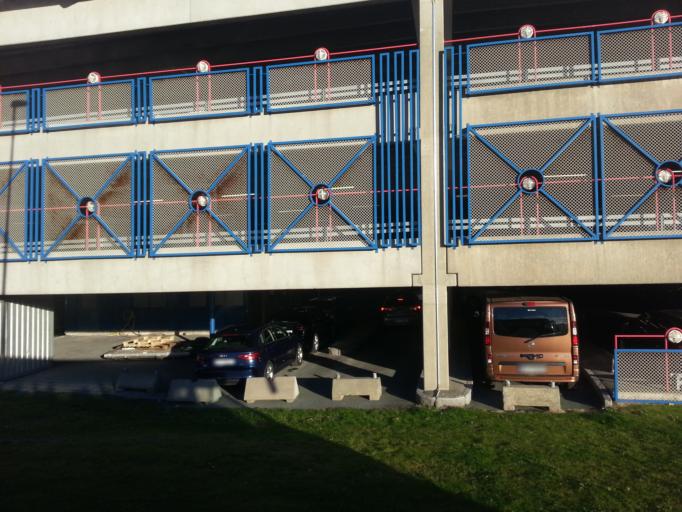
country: NO
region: Nord-Trondelag
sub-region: Stjordal
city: Stjordal
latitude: 63.4534
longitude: 10.9150
